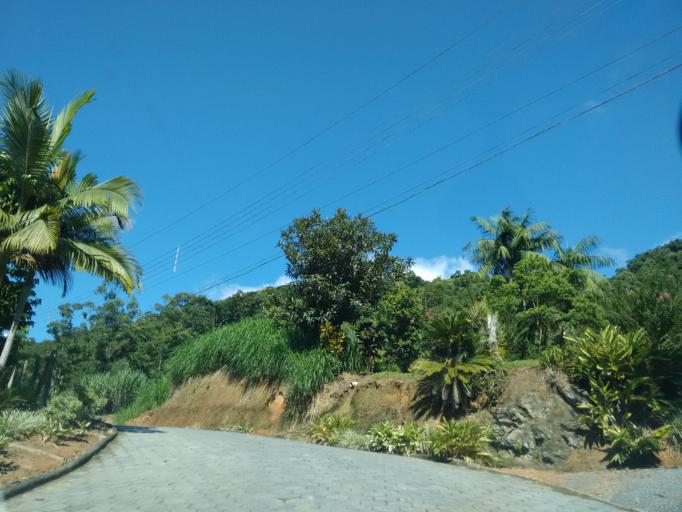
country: BR
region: Santa Catarina
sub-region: Pomerode
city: Pomerode
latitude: -26.7503
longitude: -49.1862
